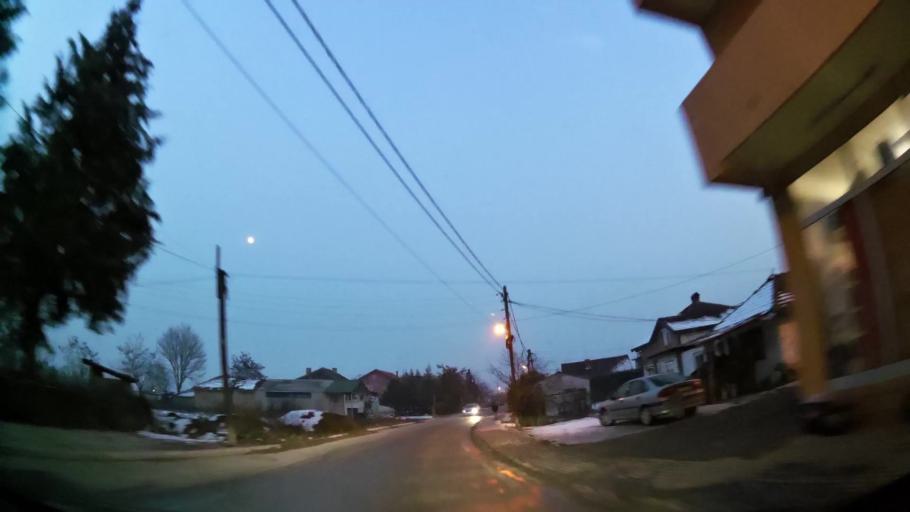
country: MK
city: Creshevo
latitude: 42.0038
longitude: 21.5170
